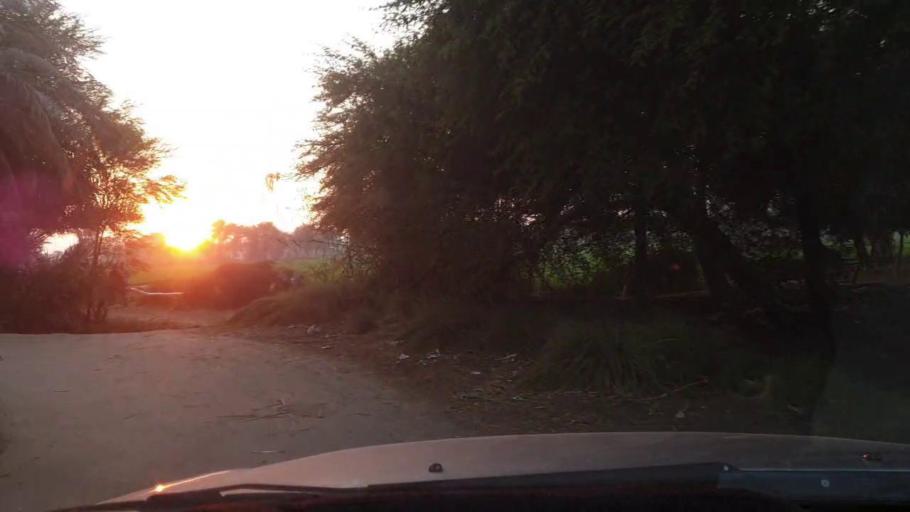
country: PK
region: Sindh
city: Mirpur Mathelo
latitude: 28.0189
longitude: 69.5650
